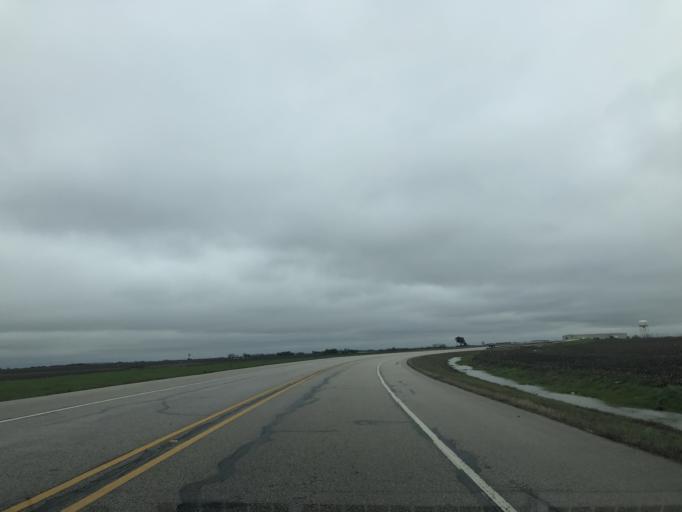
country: US
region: Texas
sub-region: Williamson County
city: Hutto
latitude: 30.6023
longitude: -97.5203
